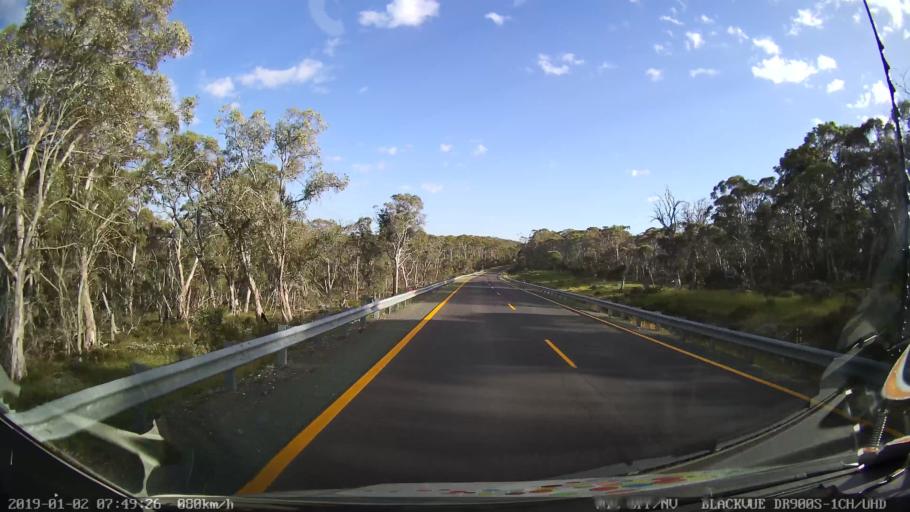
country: AU
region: New South Wales
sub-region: Tumut Shire
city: Tumut
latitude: -35.7417
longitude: 148.5223
